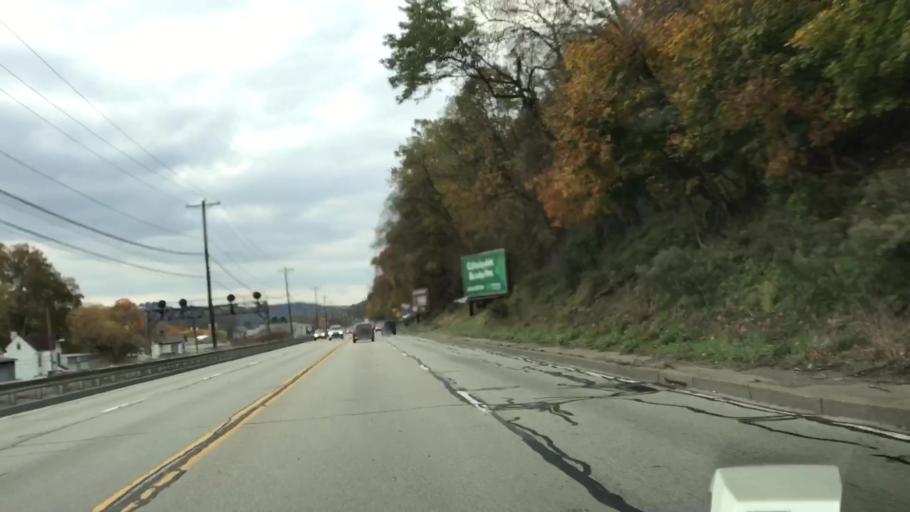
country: US
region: Pennsylvania
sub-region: Allegheny County
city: Coraopolis
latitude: 40.5243
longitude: -80.1531
